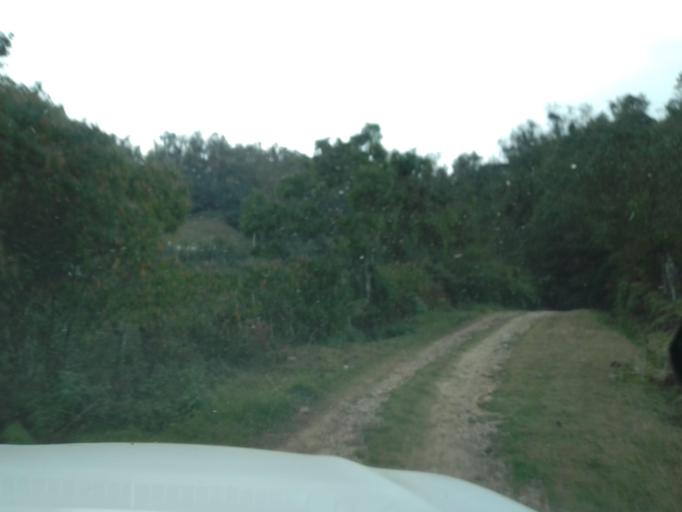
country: MX
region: Chiapas
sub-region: Cacahoatan
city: Benito Juarez
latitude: 15.2070
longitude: -92.2217
